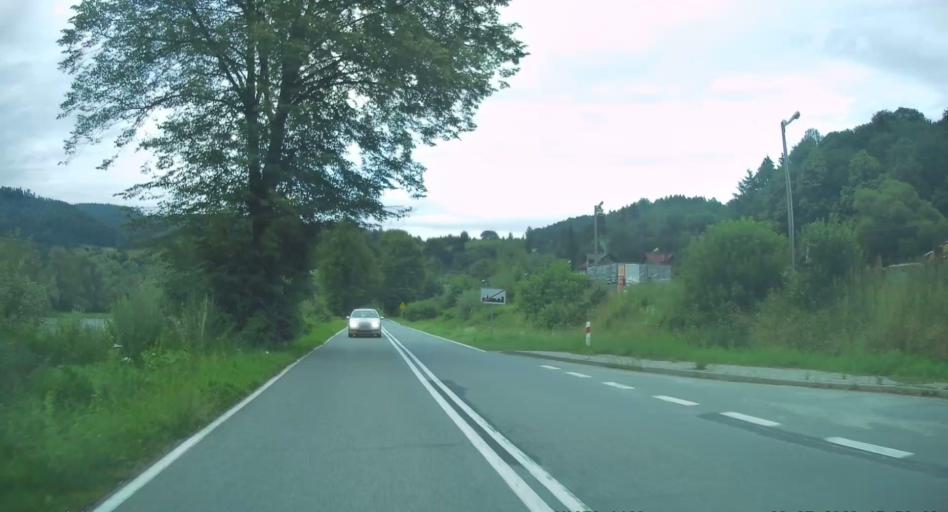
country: PL
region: Lesser Poland Voivodeship
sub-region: Powiat nowosadecki
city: Piwniczna-Zdroj
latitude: 49.3688
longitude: 20.7858
